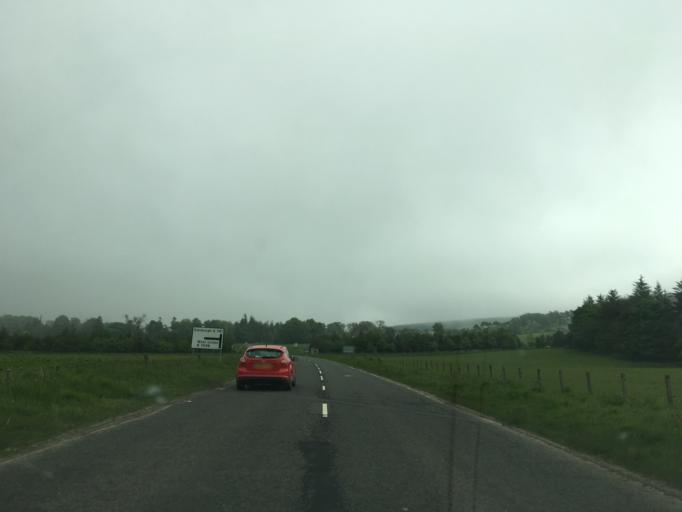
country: GB
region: Scotland
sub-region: The Scottish Borders
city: West Linton
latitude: 55.7271
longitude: -3.3213
